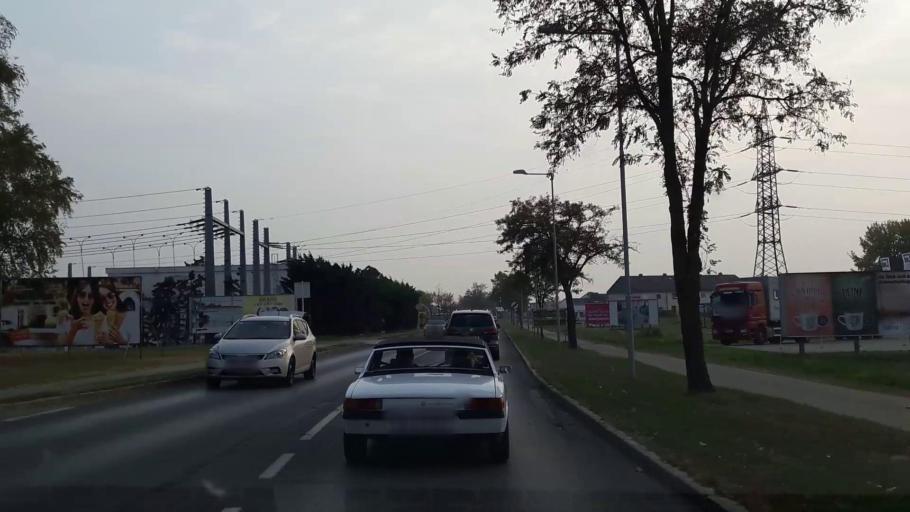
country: AT
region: Burgenland
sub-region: Politischer Bezirk Neusiedl am See
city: Neusiedl am See
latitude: 47.9617
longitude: 16.8364
